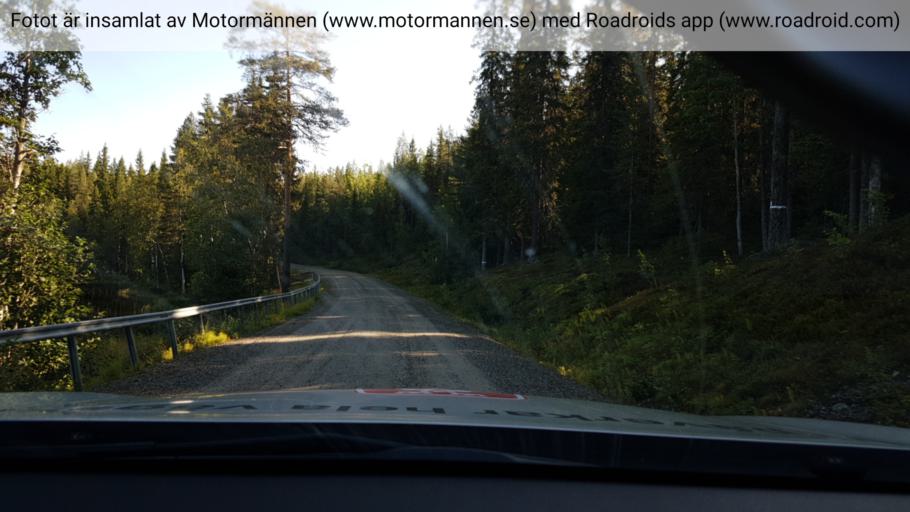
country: SE
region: Vaesterbotten
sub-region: Norsjo Kommun
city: Norsjoe
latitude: 64.7045
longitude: 19.5241
